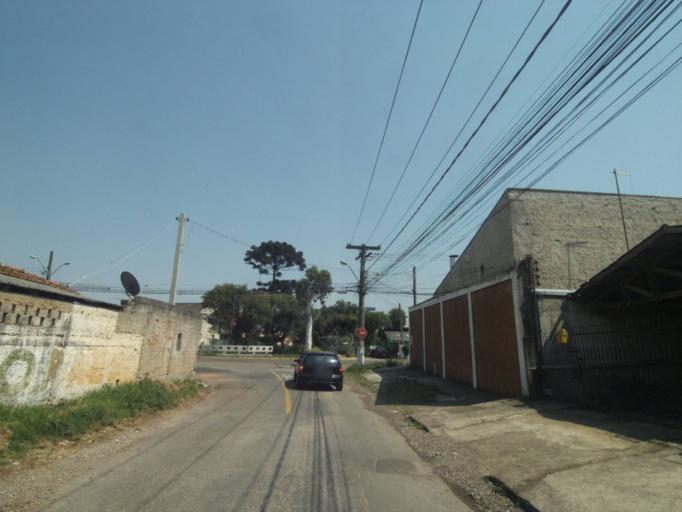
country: BR
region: Parana
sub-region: Sao Jose Dos Pinhais
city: Sao Jose dos Pinhais
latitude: -25.5103
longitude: -49.2735
